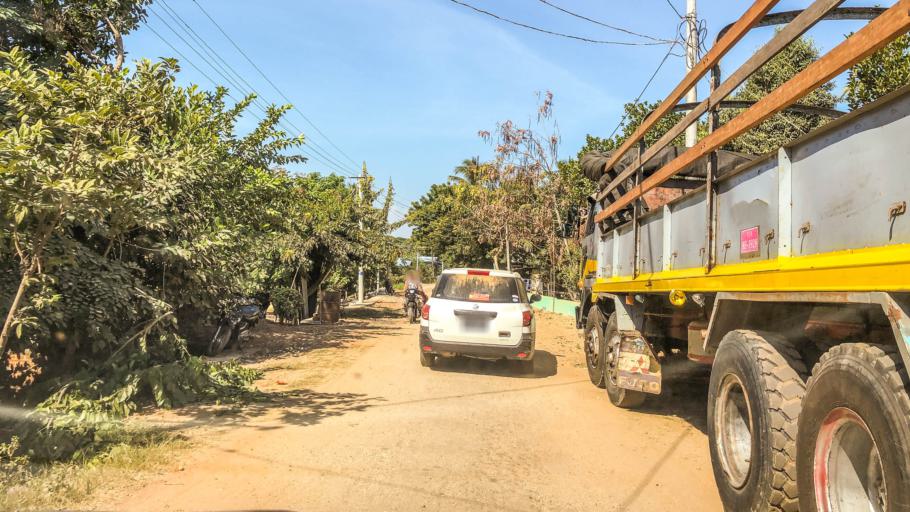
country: MM
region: Magway
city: Magway
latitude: 19.9707
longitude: 95.0429
